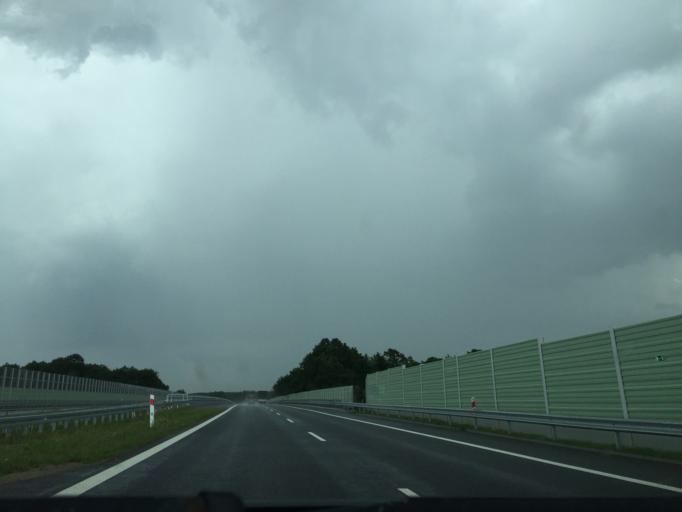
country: PL
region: Masovian Voivodeship
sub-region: Powiat szydlowiecki
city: Oronsko
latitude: 51.3088
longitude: 21.0072
